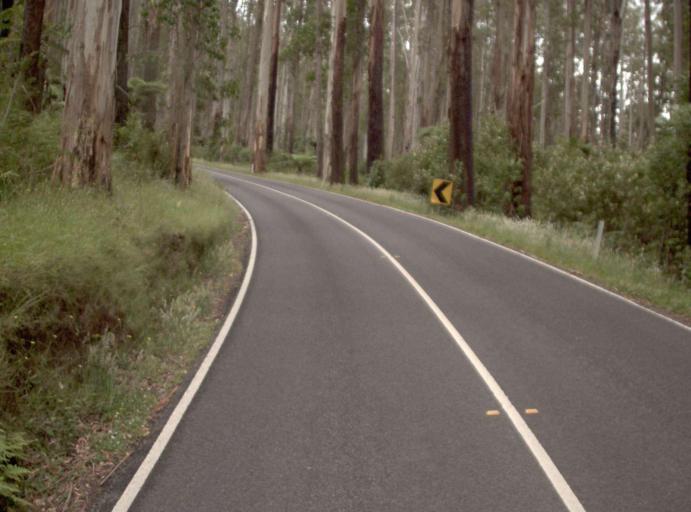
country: AU
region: Victoria
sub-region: Yarra Ranges
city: Healesville
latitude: -37.6132
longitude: 145.6054
